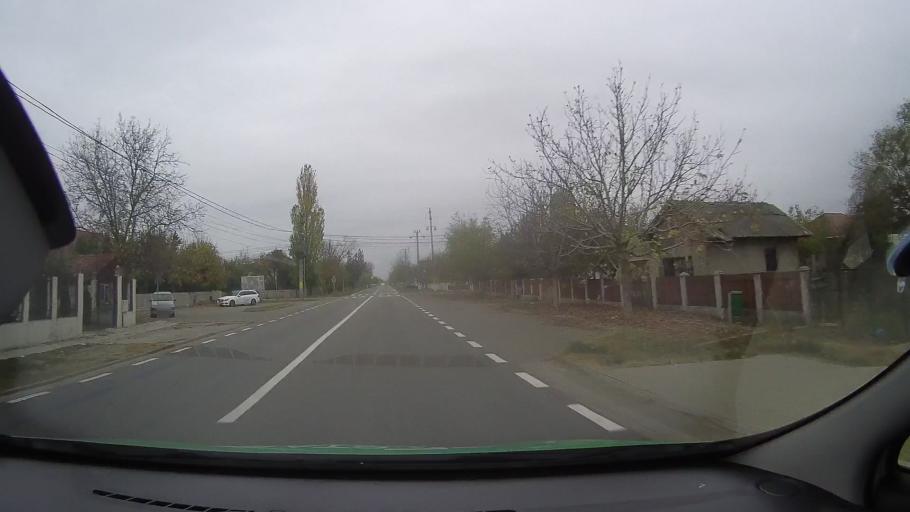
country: RO
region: Ialomita
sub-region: Comuna Slobozia
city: Slobozia
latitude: 44.6029
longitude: 27.3873
